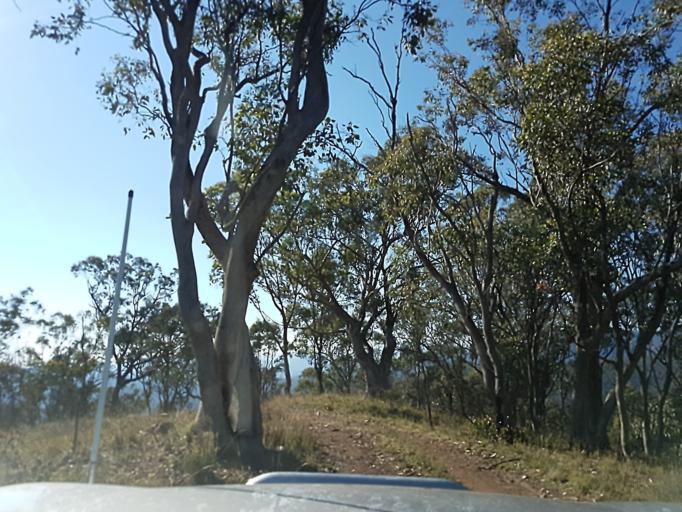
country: AU
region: New South Wales
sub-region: Snowy River
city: Jindabyne
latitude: -36.9810
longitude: 148.3066
